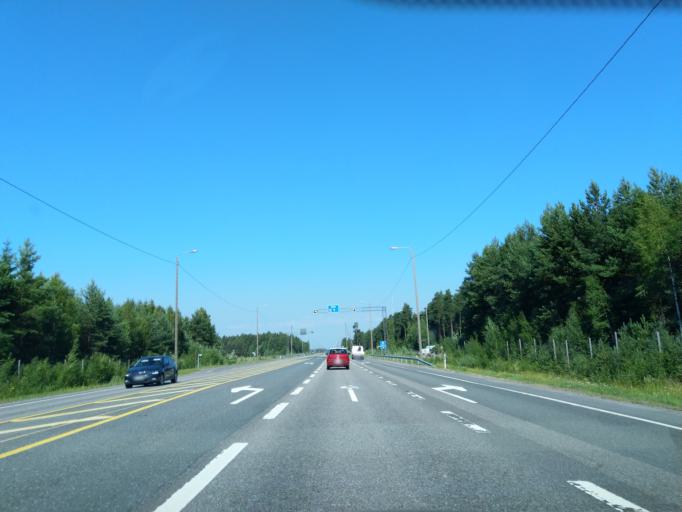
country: FI
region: Satakunta
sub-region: Pori
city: Nakkila
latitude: 61.3316
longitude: 22.0608
